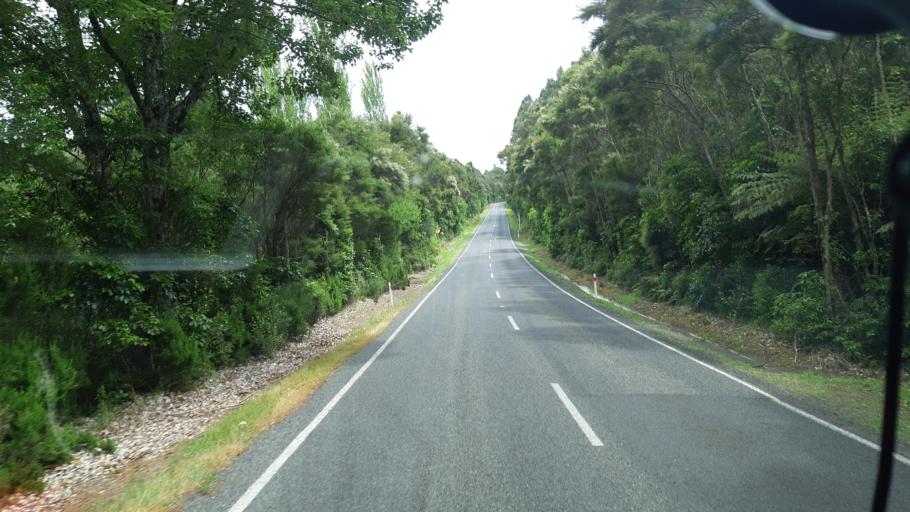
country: NZ
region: Waikato
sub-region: South Waikato District
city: Tokoroa
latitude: -38.2739
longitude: 175.6689
